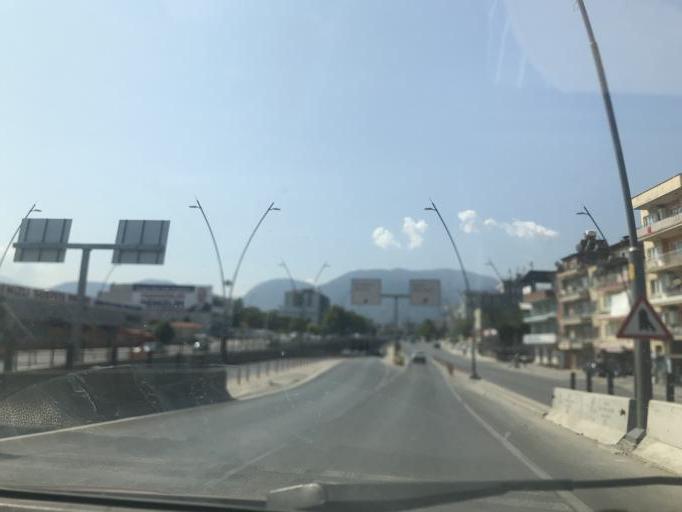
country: TR
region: Denizli
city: Denizli
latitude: 37.7810
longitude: 29.0970
